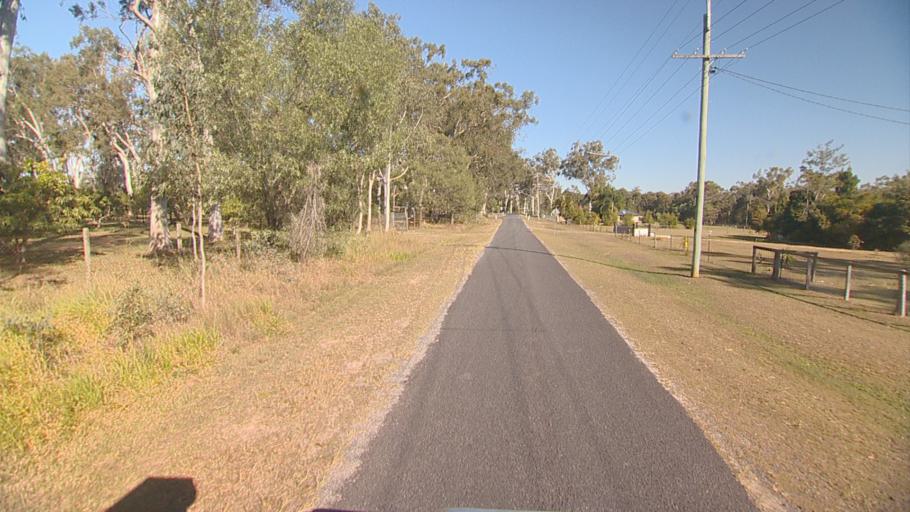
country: AU
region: Queensland
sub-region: Logan
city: Logan Reserve
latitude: -27.7316
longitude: 153.0780
